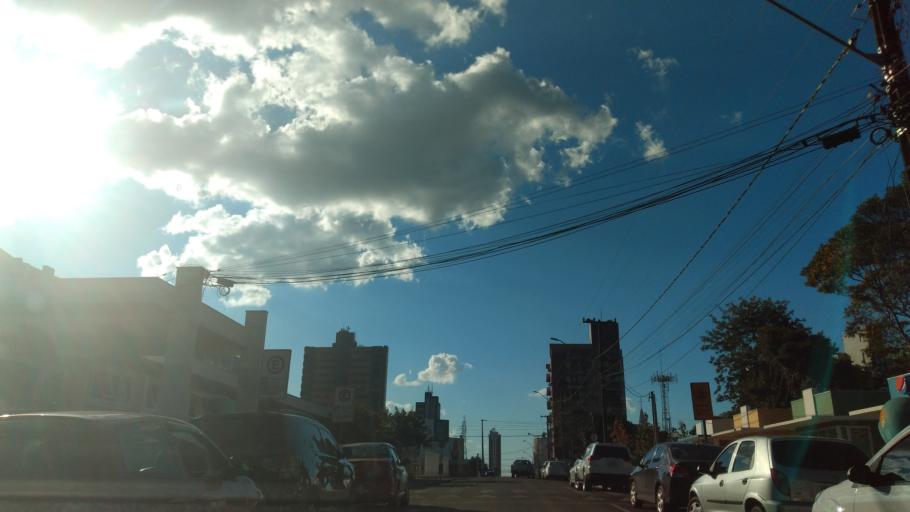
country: BR
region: Parana
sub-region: Guarapuava
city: Guarapuava
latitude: -25.3965
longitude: -51.4628
